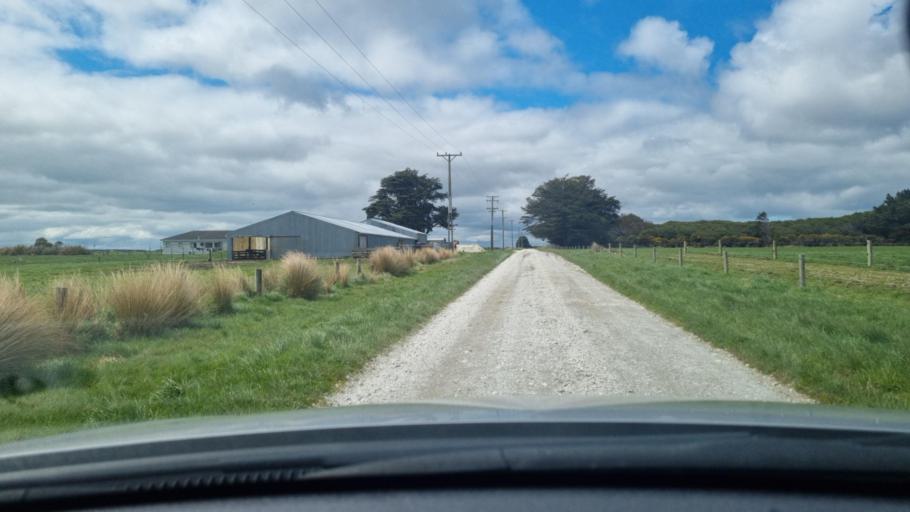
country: NZ
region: Southland
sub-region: Invercargill City
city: Invercargill
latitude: -46.5067
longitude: 168.4361
